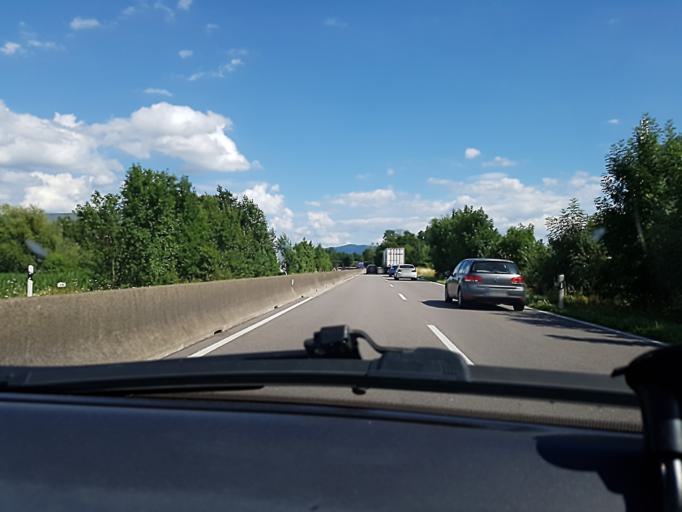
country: DE
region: Baden-Wuerttemberg
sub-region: Freiburg Region
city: Willstatt
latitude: 48.5422
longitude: 7.9045
